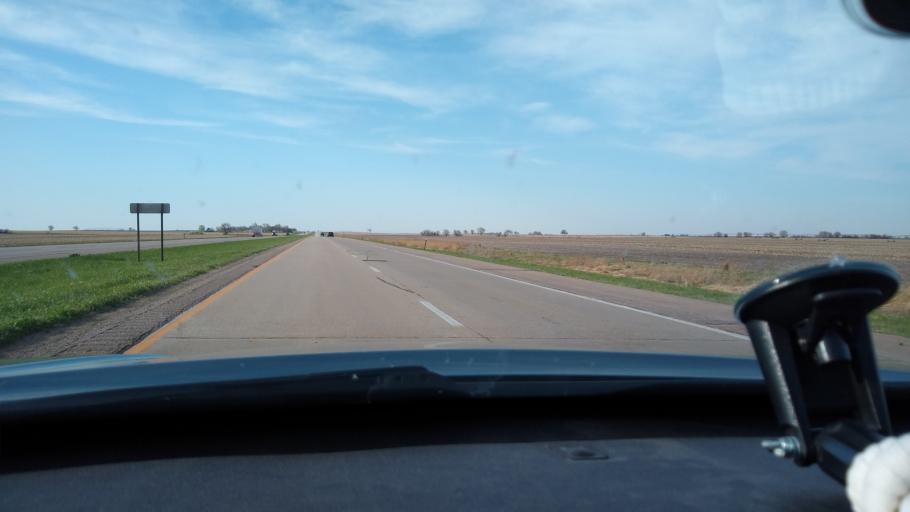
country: US
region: Nebraska
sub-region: Fillmore County
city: Geneva
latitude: 40.6710
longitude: -97.5957
